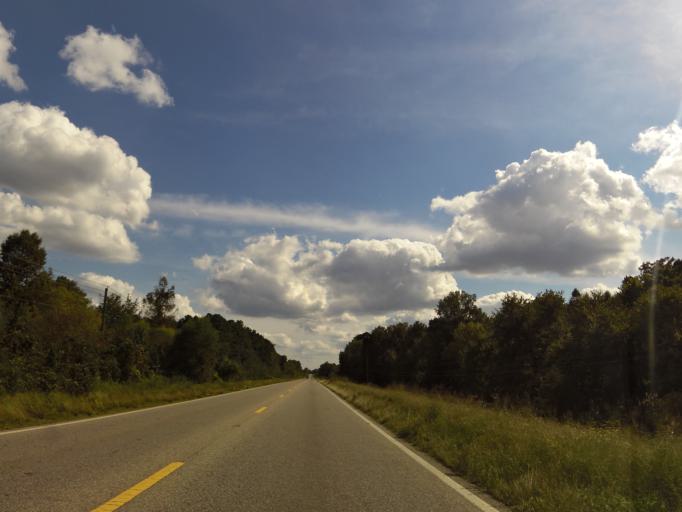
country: US
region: Alabama
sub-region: Dallas County
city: Selmont-West Selmont
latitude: 32.3552
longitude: -87.0017
